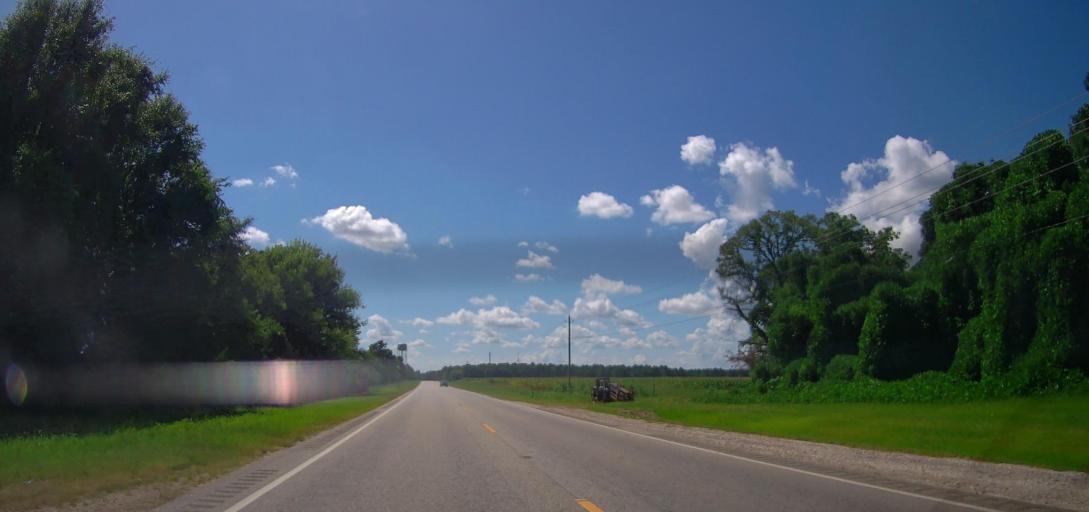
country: US
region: Alabama
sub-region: Elmore County
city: Tallassee
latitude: 32.3928
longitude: -85.9009
